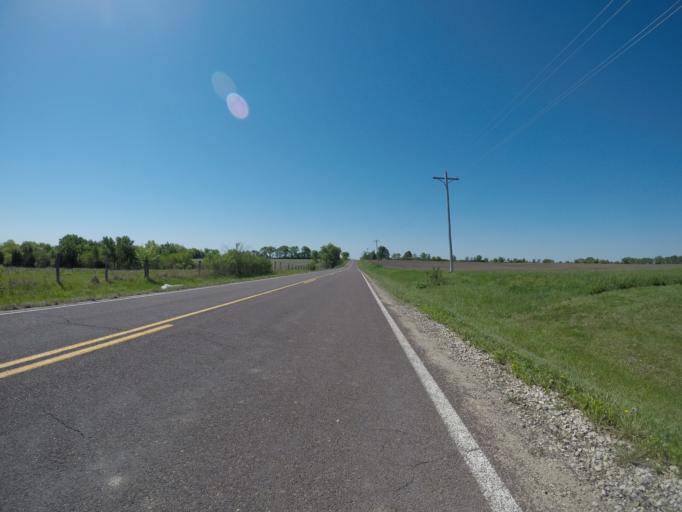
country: US
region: Kansas
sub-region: Osage County
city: Overbrook
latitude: 38.8544
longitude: -95.4821
